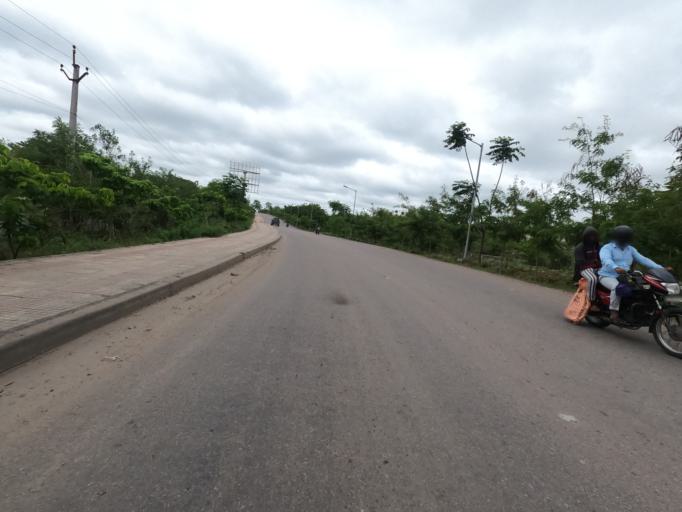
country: IN
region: Telangana
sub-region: Hyderabad
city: Hyderabad
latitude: 17.3485
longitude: 78.3613
